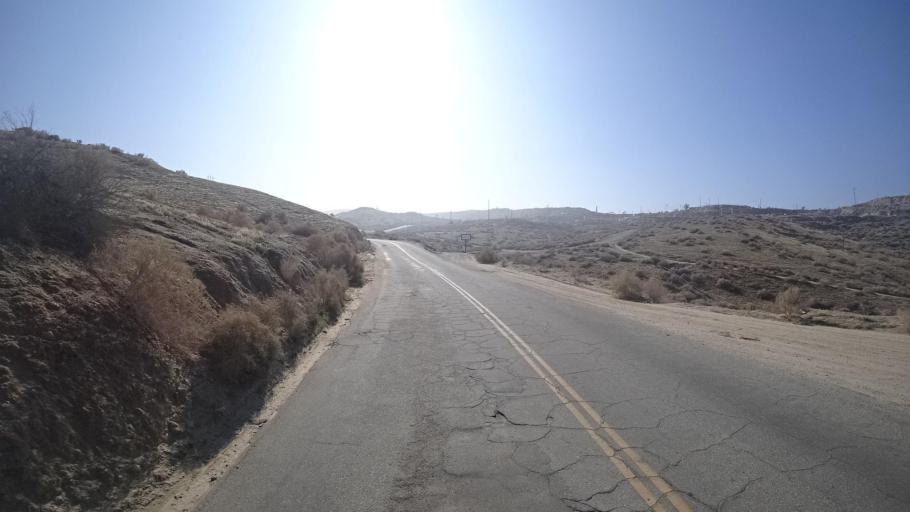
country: US
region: California
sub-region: Kern County
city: Taft Heights
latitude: 35.1250
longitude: -119.4727
